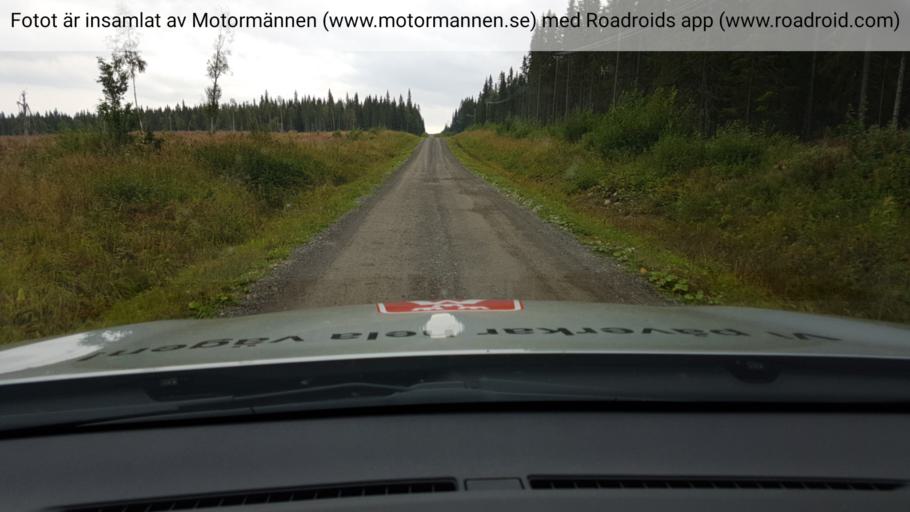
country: SE
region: Jaemtland
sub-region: Stroemsunds Kommun
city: Stroemsund
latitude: 63.7840
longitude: 15.3052
